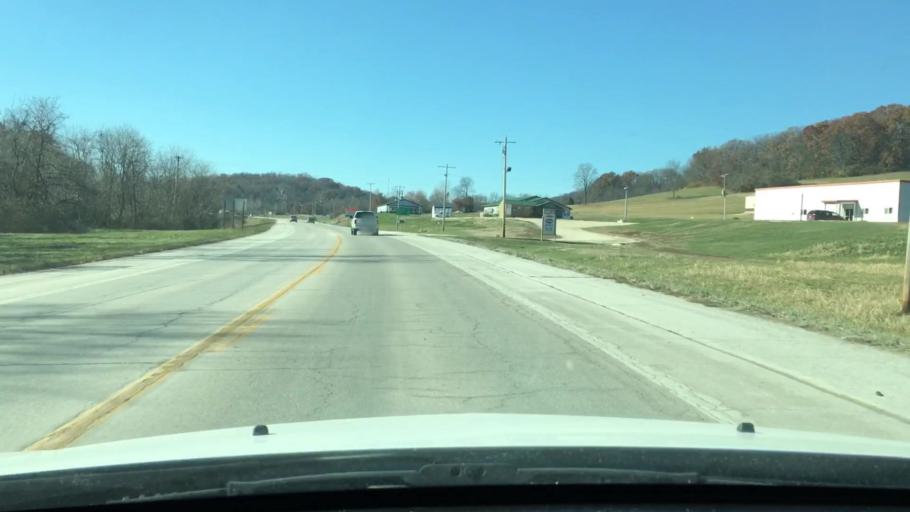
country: US
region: Missouri
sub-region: Pike County
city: Louisiana
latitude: 39.4517
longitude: -91.0632
